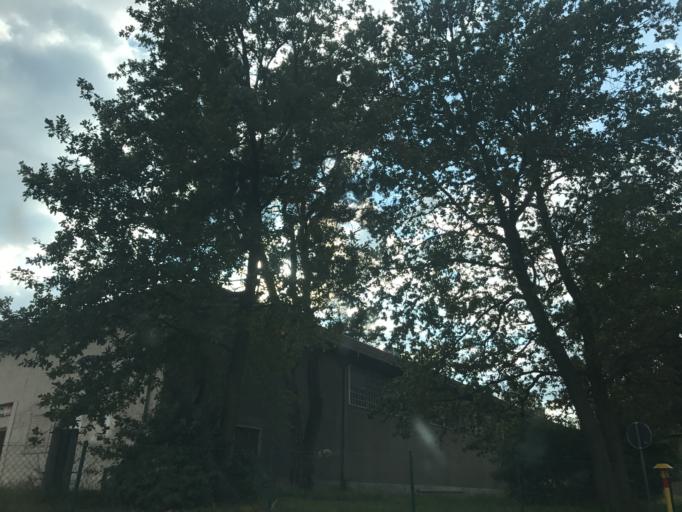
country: DE
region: Brandenburg
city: Brieselang
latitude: 52.5401
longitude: 13.0130
